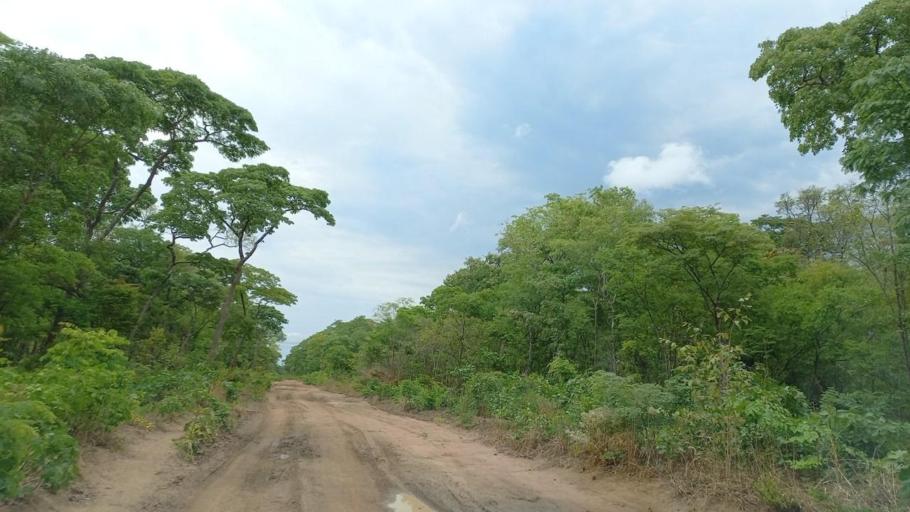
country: ZM
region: North-Western
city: Kalengwa
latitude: -13.5432
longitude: 24.9770
